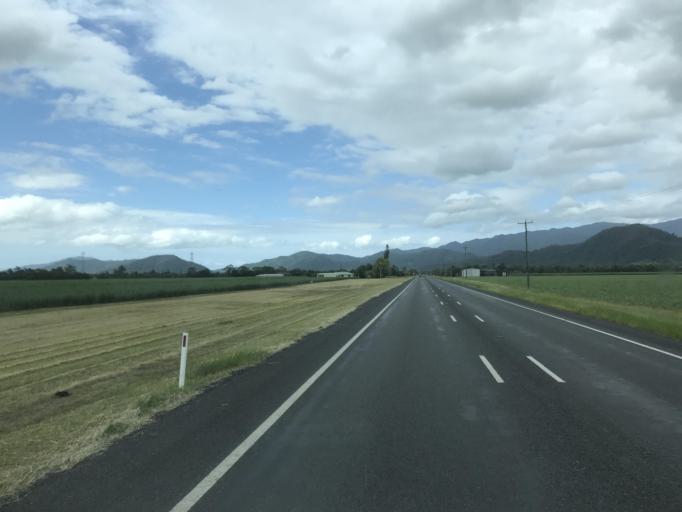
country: AU
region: Queensland
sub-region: Cassowary Coast
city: Innisfail
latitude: -17.7839
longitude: 146.0252
